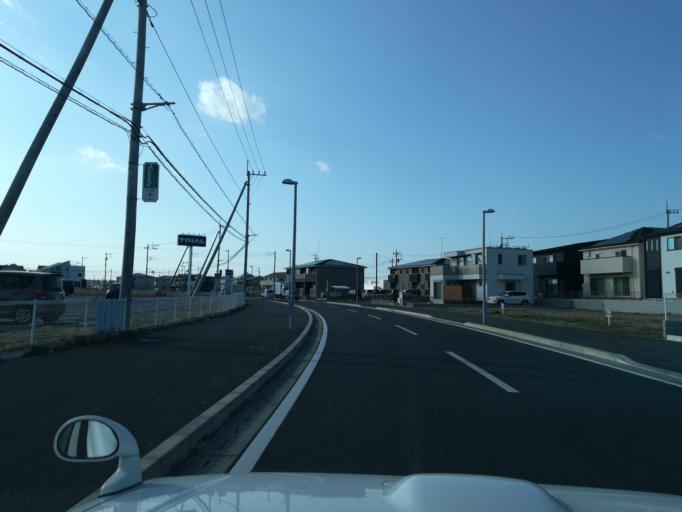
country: JP
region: Ibaraki
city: Naka
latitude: 36.0965
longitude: 140.0876
